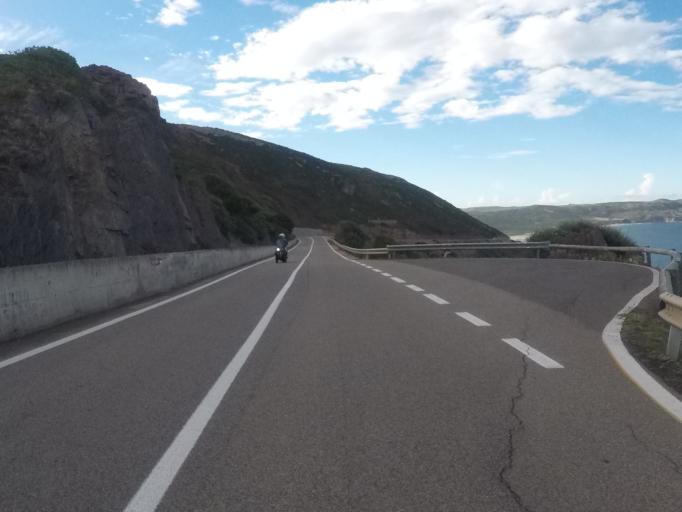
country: IT
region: Sardinia
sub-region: Provincia di Carbonia-Iglesias
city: Gonnesa
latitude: 39.3048
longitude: 8.4361
